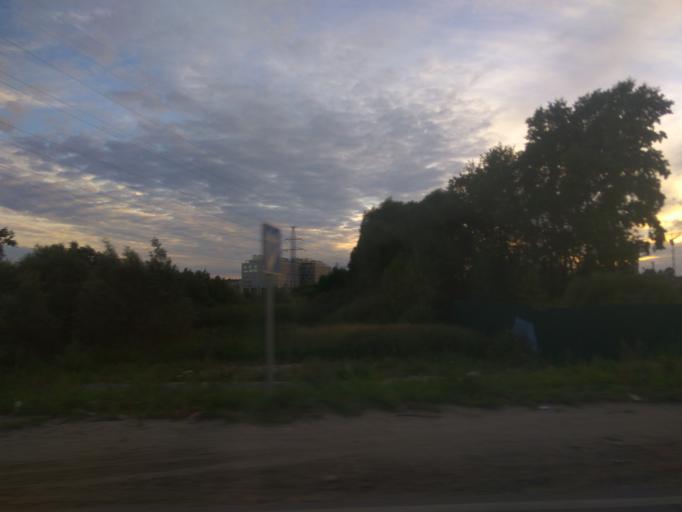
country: RU
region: Moscow
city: Solntsevo
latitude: 55.6308
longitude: 37.4208
